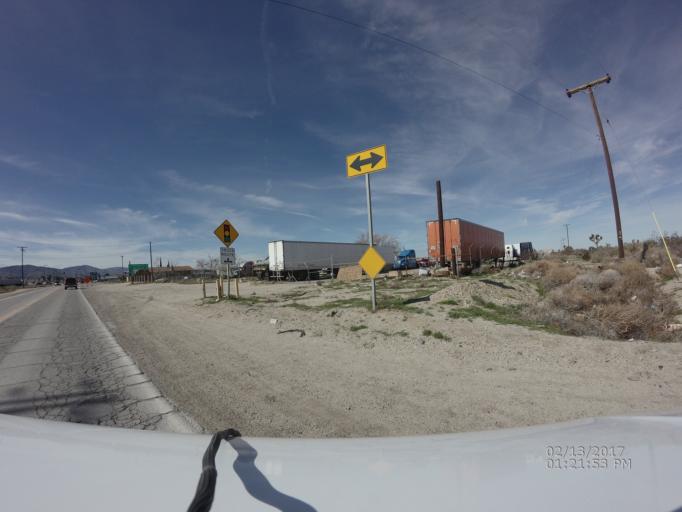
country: US
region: California
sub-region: Los Angeles County
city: Littlerock
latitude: 34.5427
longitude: -118.0278
